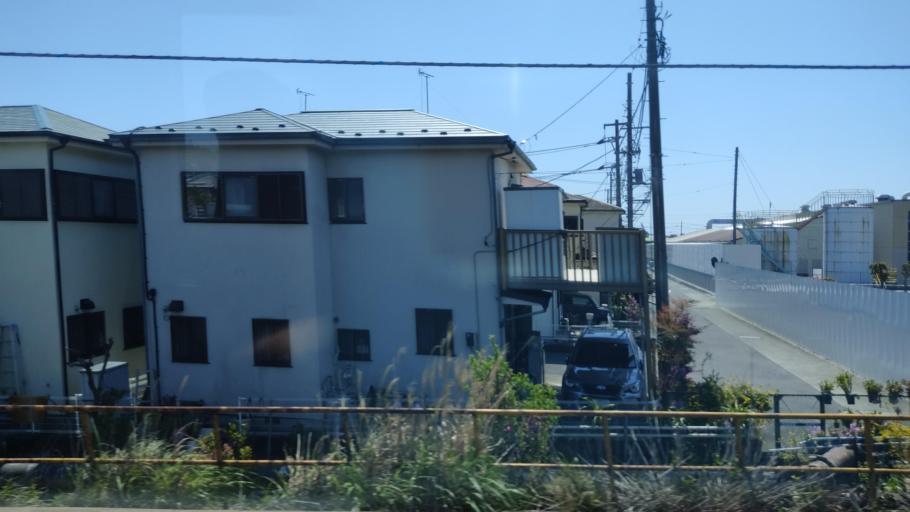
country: JP
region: Kanagawa
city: Odawara
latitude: 35.2784
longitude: 139.1964
